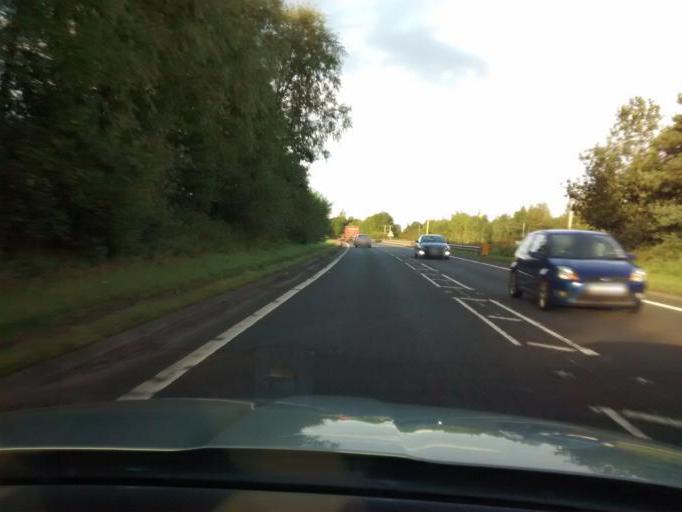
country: GB
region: Scotland
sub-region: Renfrewshire
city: Howwood
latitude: 55.8131
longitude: -4.5577
